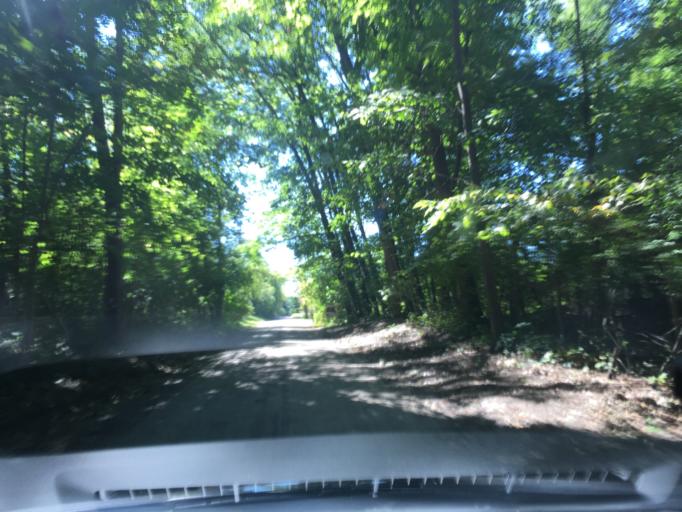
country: US
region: Michigan
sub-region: Oakland County
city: Sylvan Lake
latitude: 42.6065
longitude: -83.3079
